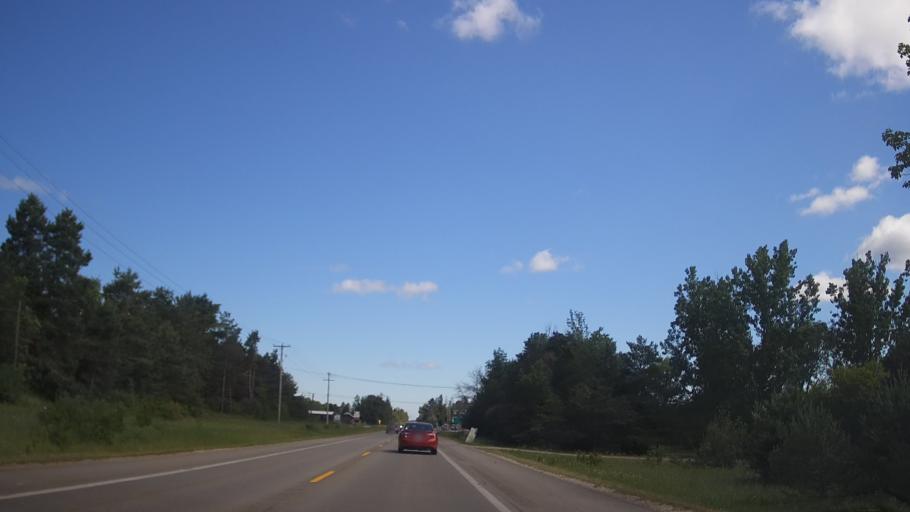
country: US
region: Michigan
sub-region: Cheboygan County
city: Indian River
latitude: 45.4901
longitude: -84.7812
